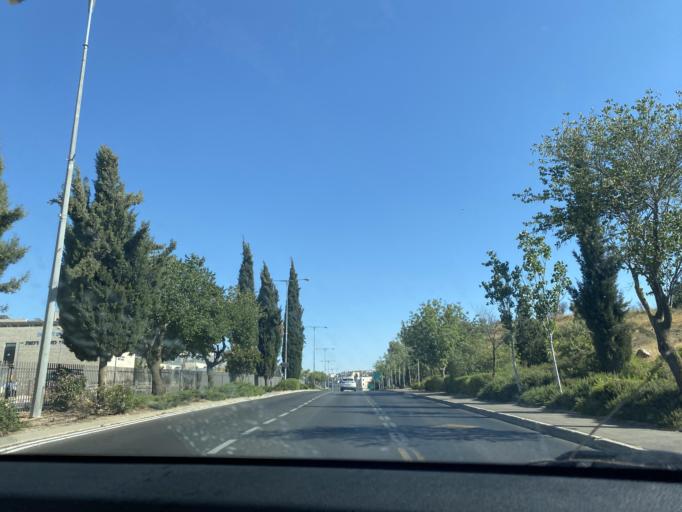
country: PS
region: West Bank
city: Bayt Iksa
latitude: 31.8242
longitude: 35.1889
